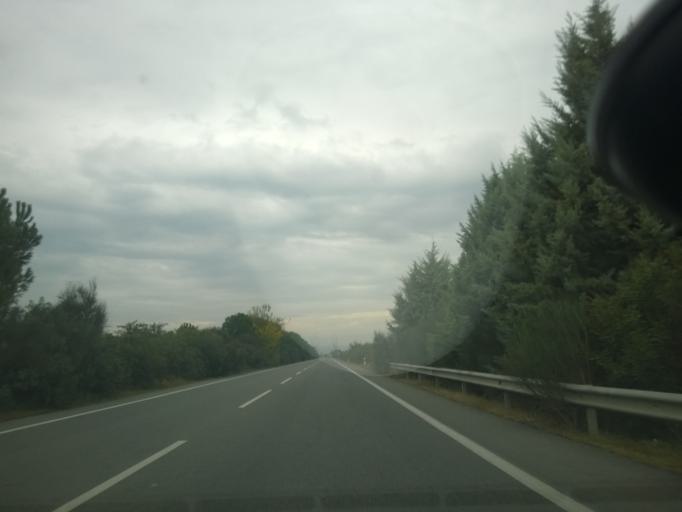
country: GR
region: Central Macedonia
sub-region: Nomos Pellis
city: Palaifyto
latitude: 40.7975
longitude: 22.2678
